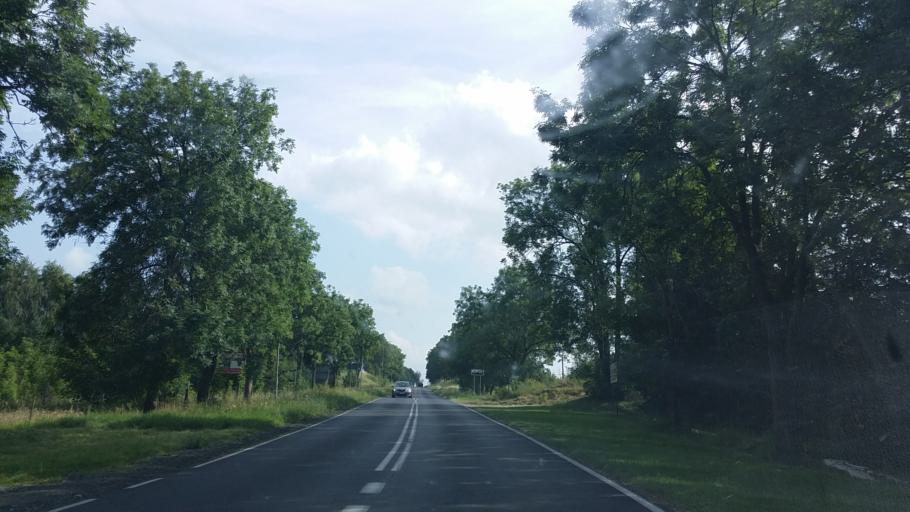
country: PL
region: West Pomeranian Voivodeship
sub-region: Powiat mysliborski
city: Barlinek
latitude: 52.9709
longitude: 15.1854
